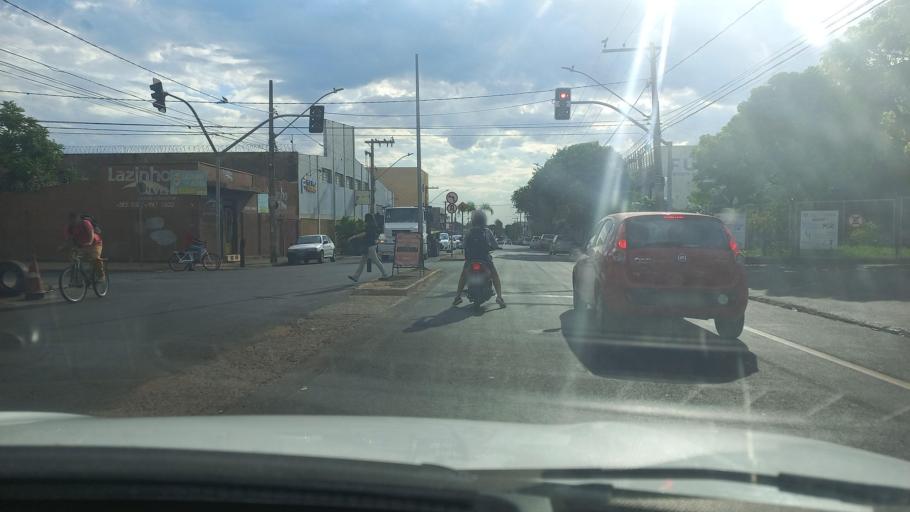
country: BR
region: Minas Gerais
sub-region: Uberaba
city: Uberaba
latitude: -19.7677
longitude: -47.9225
